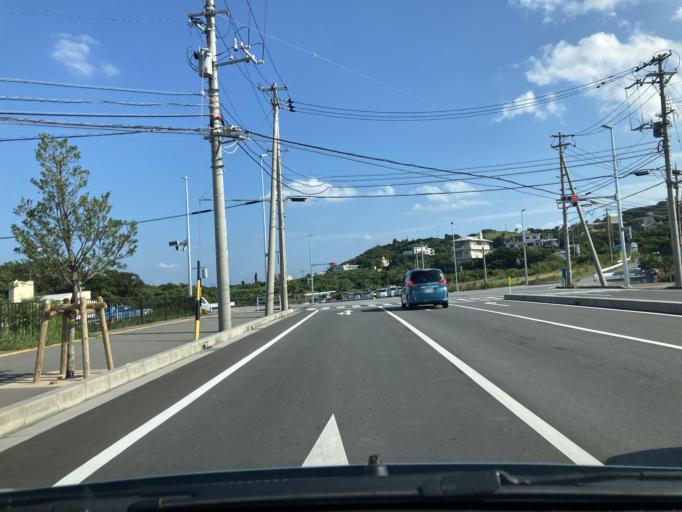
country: JP
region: Okinawa
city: Chatan
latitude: 26.2995
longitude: 127.7975
